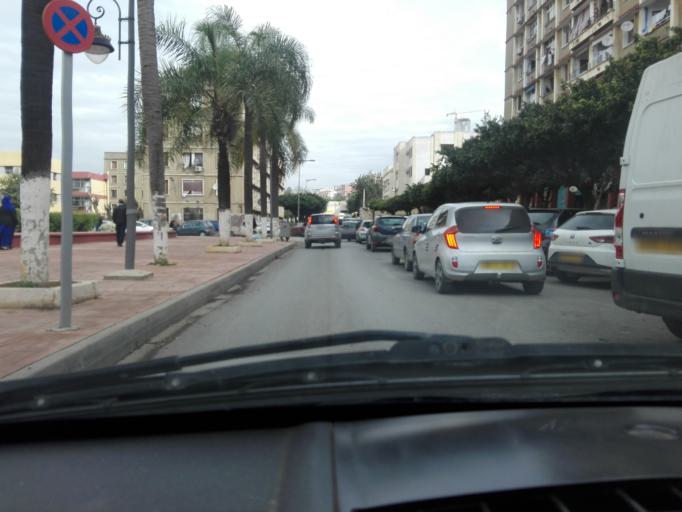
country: DZ
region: Alger
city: Bab Ezzouar
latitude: 36.7232
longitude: 3.1370
